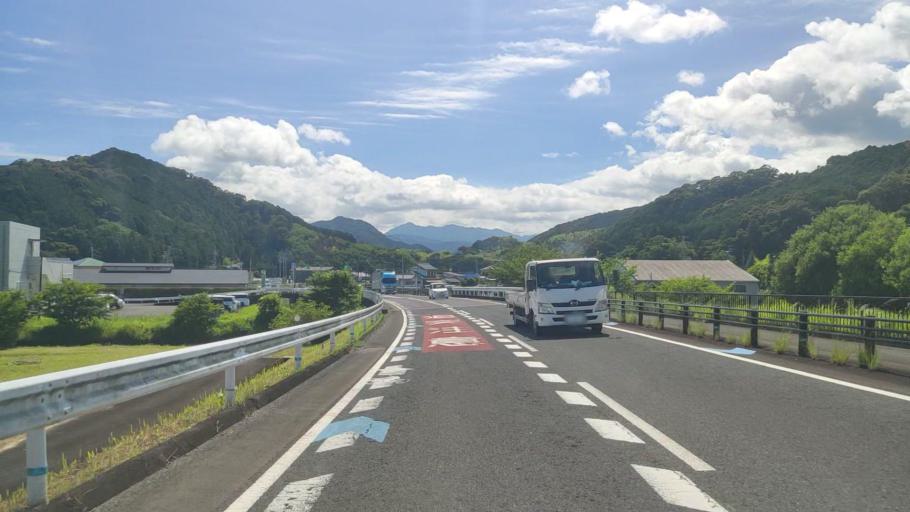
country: JP
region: Wakayama
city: Shingu
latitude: 33.7418
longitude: 136.0046
